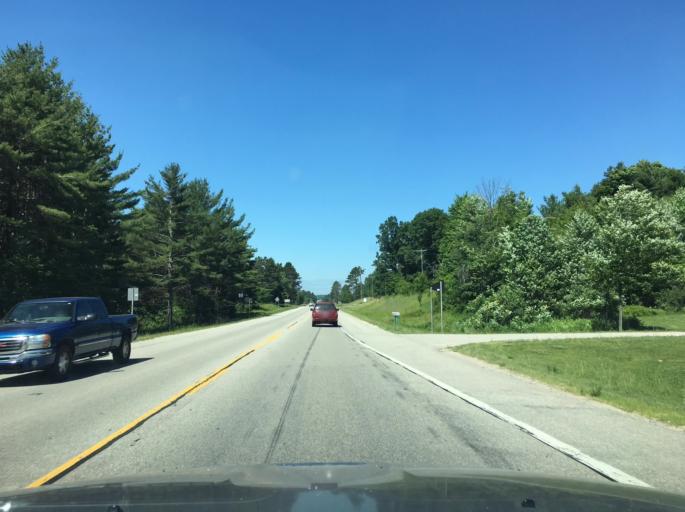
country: US
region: Michigan
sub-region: Osceola County
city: Reed City
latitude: 43.8725
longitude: -85.4453
